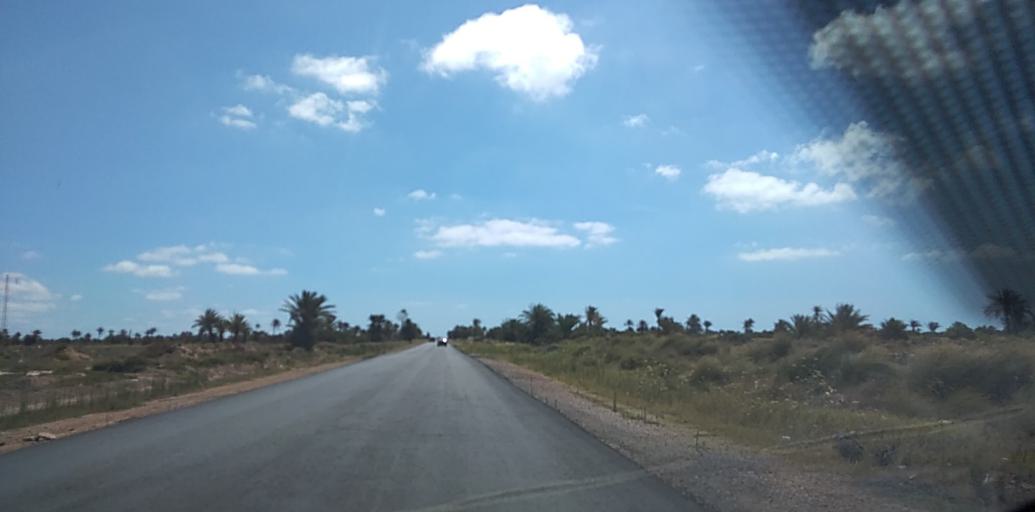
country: TN
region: Safaqis
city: Al Qarmadah
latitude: 34.6592
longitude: 11.1086
